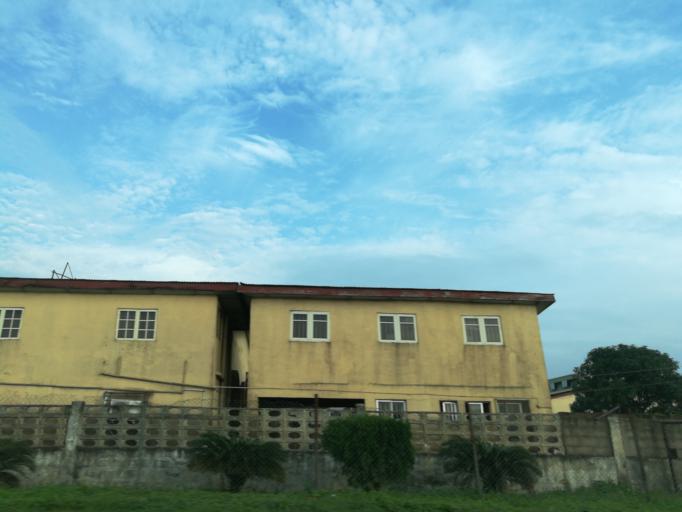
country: NG
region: Lagos
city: Oshodi
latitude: 6.5672
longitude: 3.3299
